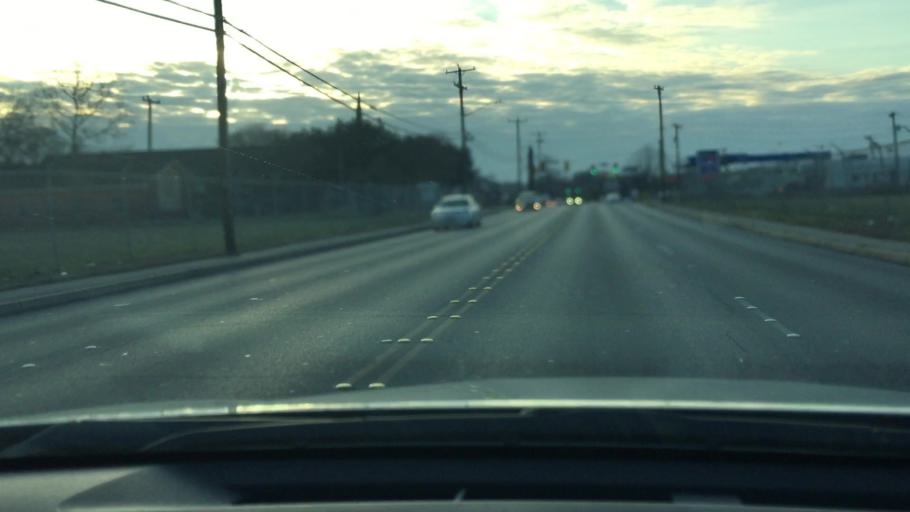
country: US
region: Texas
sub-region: Bexar County
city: Terrell Hills
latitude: 29.4966
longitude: -98.4171
